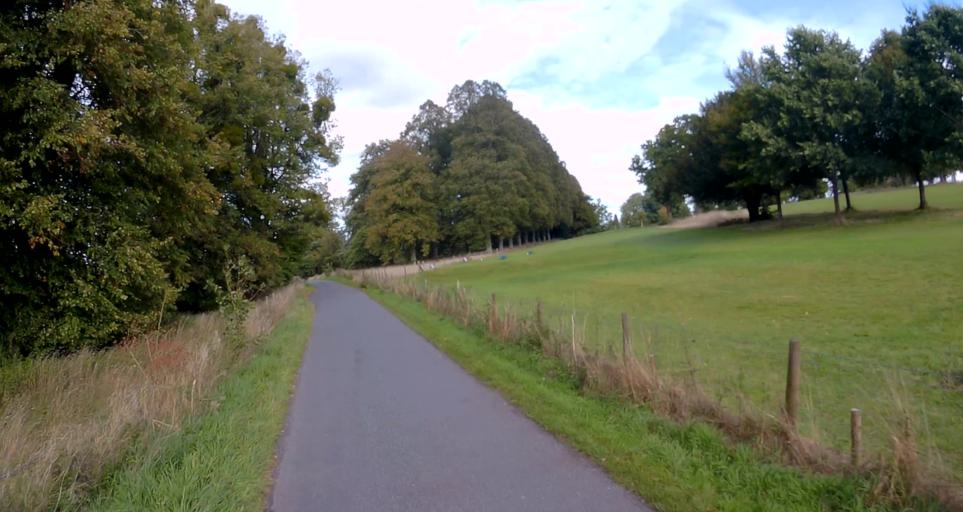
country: GB
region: England
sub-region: Hampshire
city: Kings Worthy
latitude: 51.0892
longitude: -1.2325
